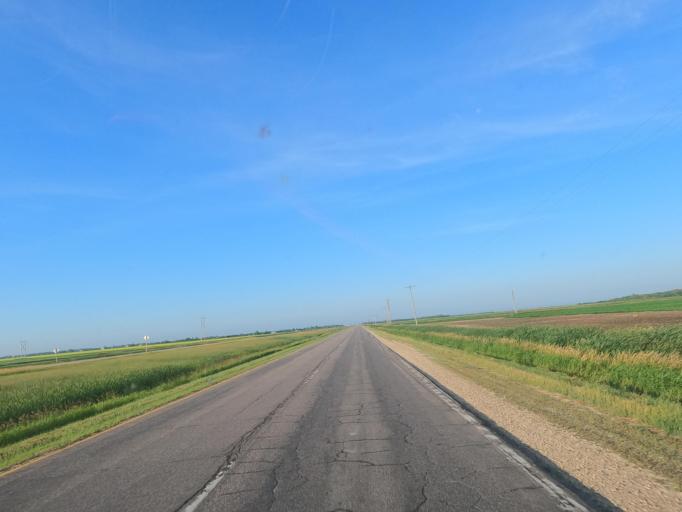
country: CA
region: Manitoba
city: Winnipeg
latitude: 50.0439
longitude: -97.0725
